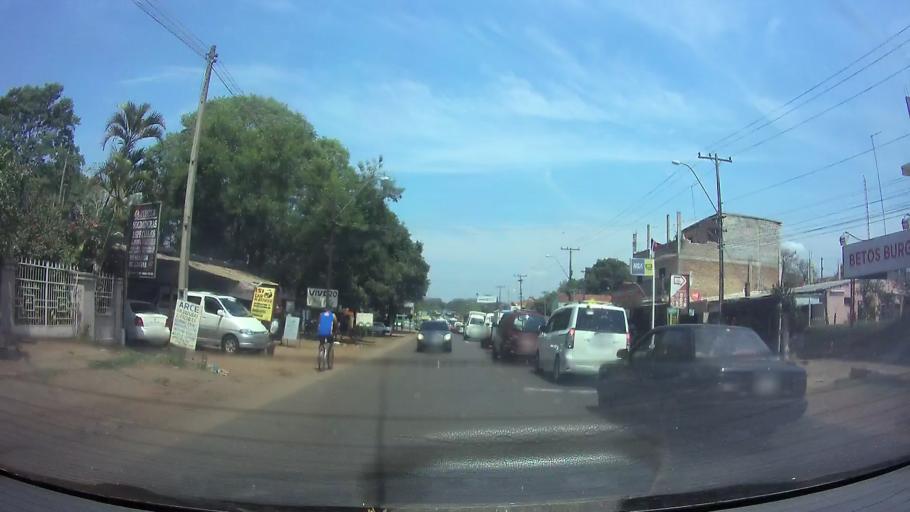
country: PY
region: Central
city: Capiata
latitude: -25.4158
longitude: -57.4569
